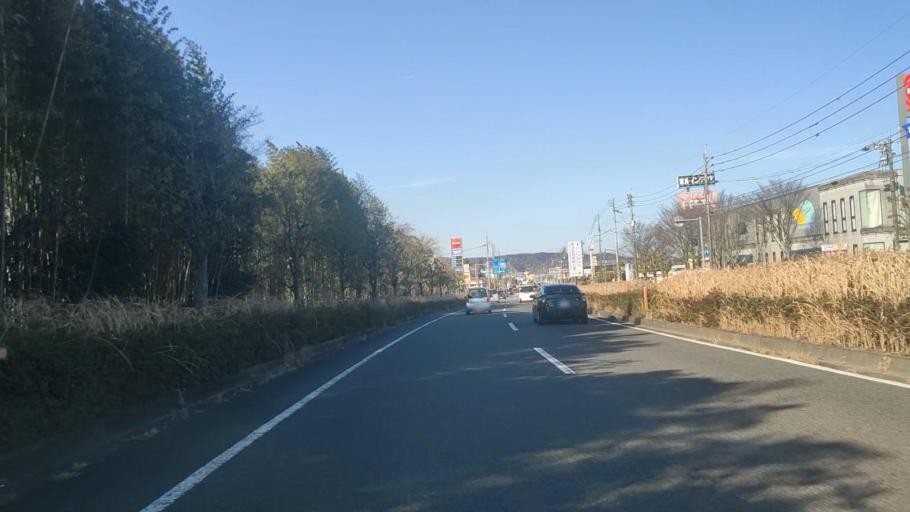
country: JP
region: Oita
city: Oita
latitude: 33.1401
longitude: 131.6582
